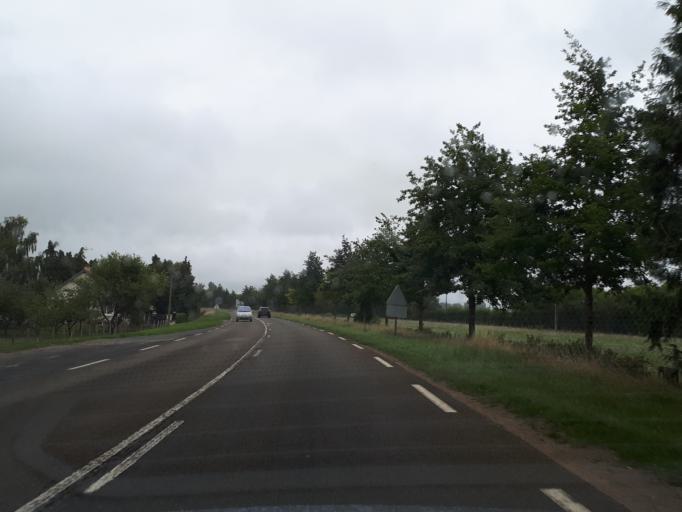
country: FR
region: Pays de la Loire
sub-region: Departement de la Sarthe
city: Champagne
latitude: 48.0785
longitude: 0.3111
